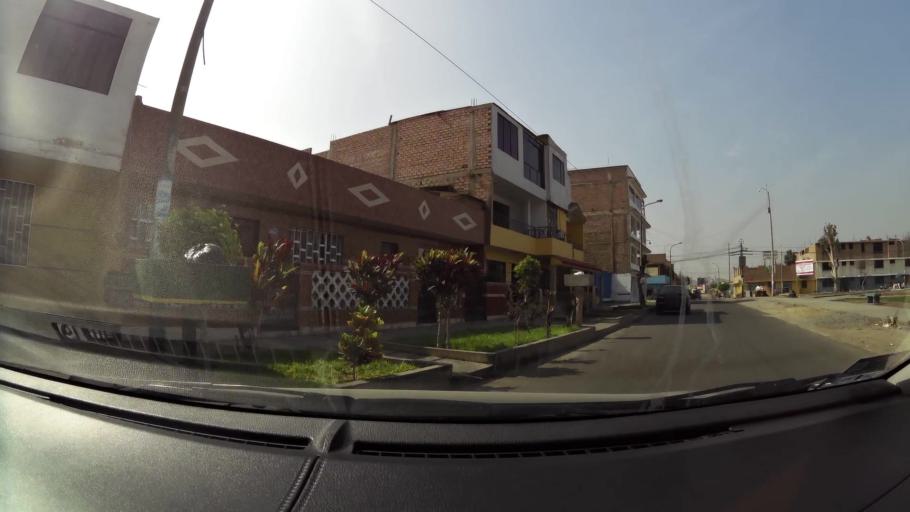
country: PE
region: Lima
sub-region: Lima
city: Santa Rosa
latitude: -11.7786
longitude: -77.1629
